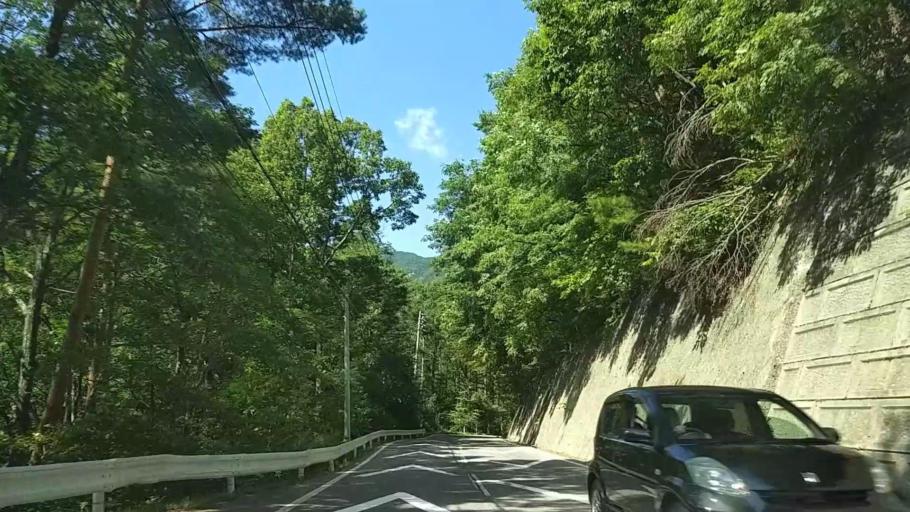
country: JP
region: Nagano
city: Matsumoto
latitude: 36.1969
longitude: 138.0707
